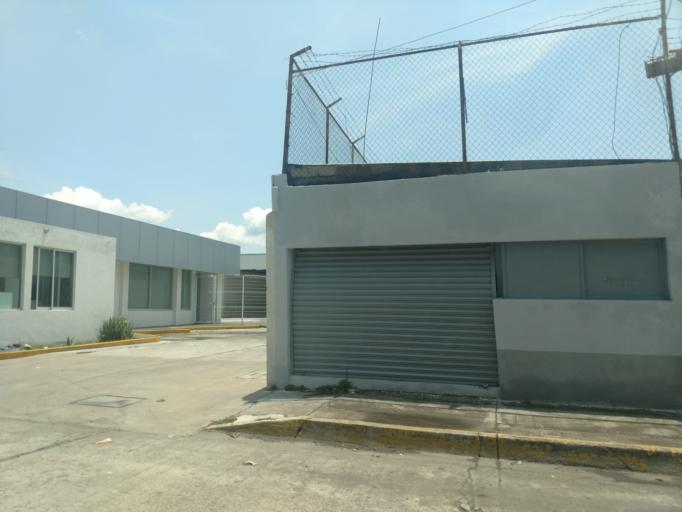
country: MX
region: Nayarit
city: Tepic
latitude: 21.5044
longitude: -104.8845
